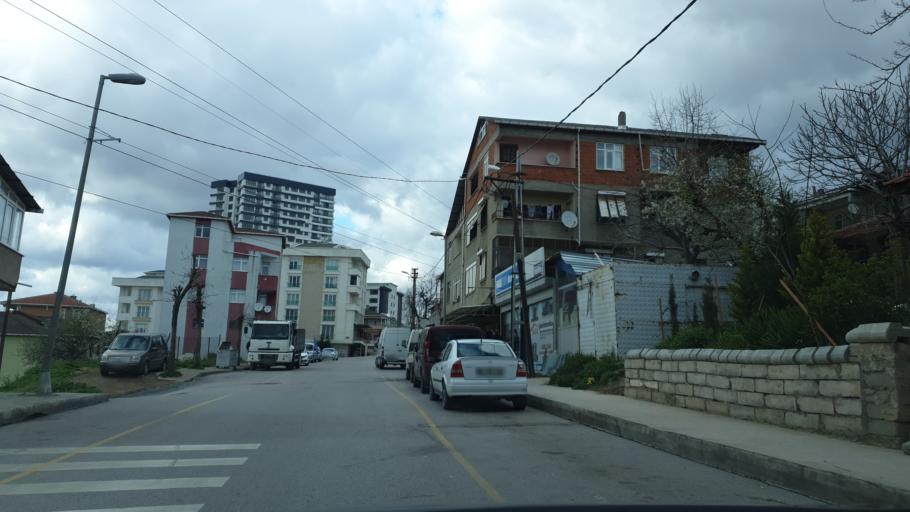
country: TR
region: Istanbul
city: Pendik
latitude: 40.8960
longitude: 29.2372
